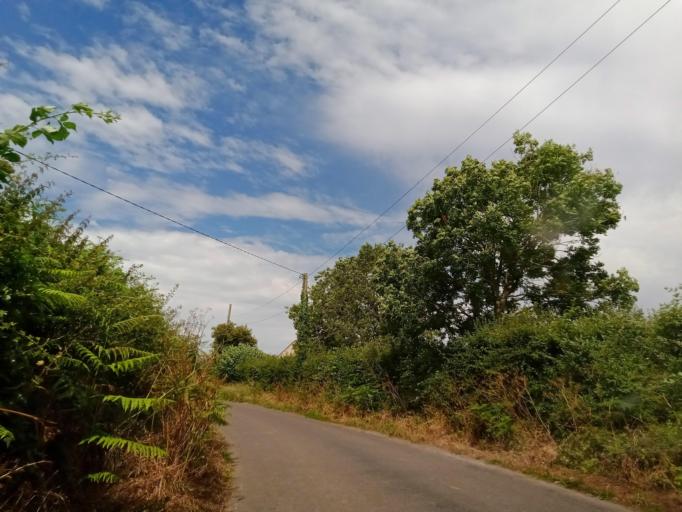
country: IE
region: Leinster
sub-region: Kilkenny
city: Thomastown
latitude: 52.5724
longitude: -7.1257
